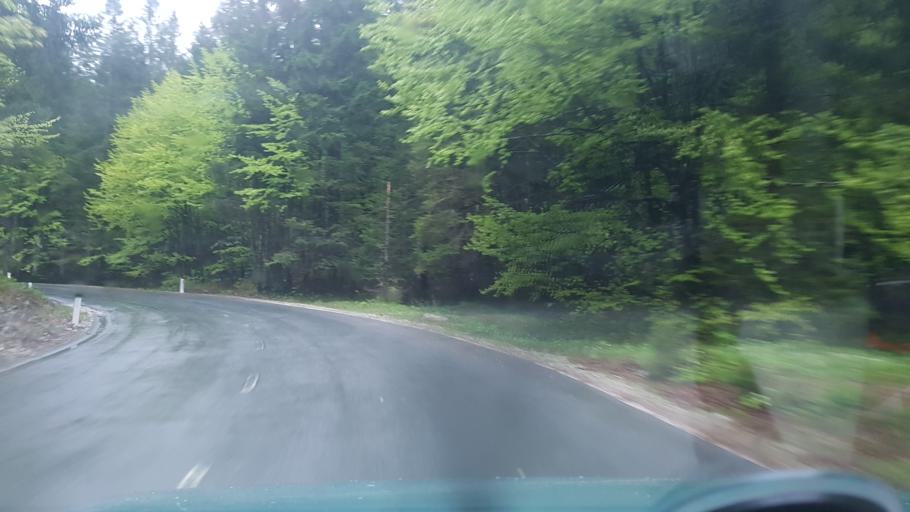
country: SI
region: Bohinj
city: Bohinjska Bistrica
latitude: 46.2437
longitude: 14.0067
